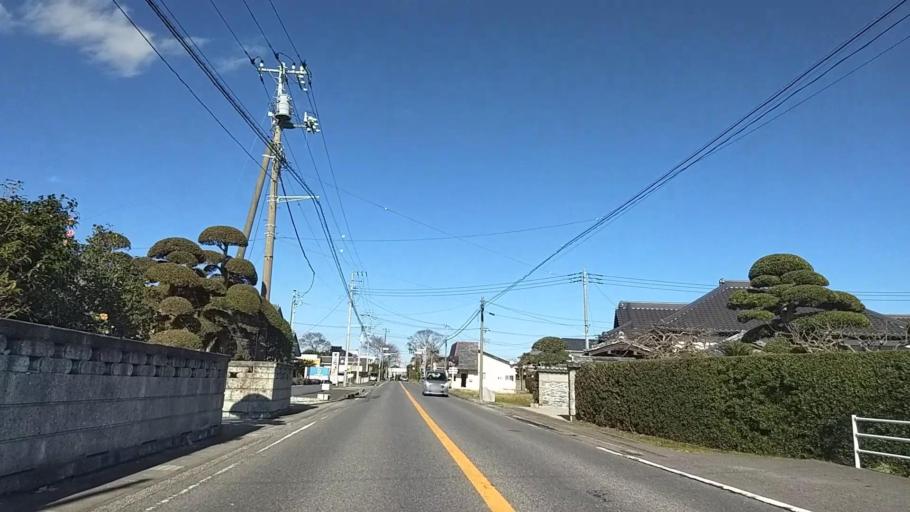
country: JP
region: Chiba
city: Ohara
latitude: 35.2432
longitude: 140.3930
